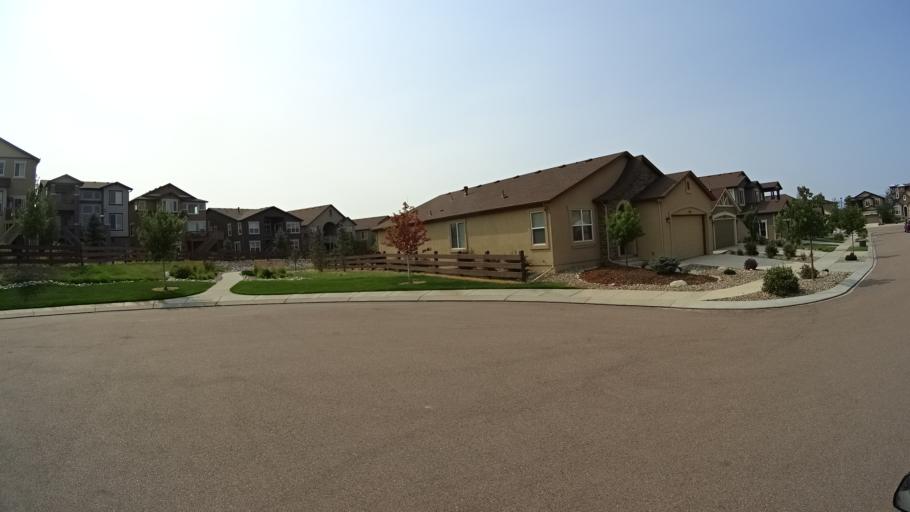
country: US
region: Colorado
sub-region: El Paso County
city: Black Forest
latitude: 38.9638
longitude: -104.7302
